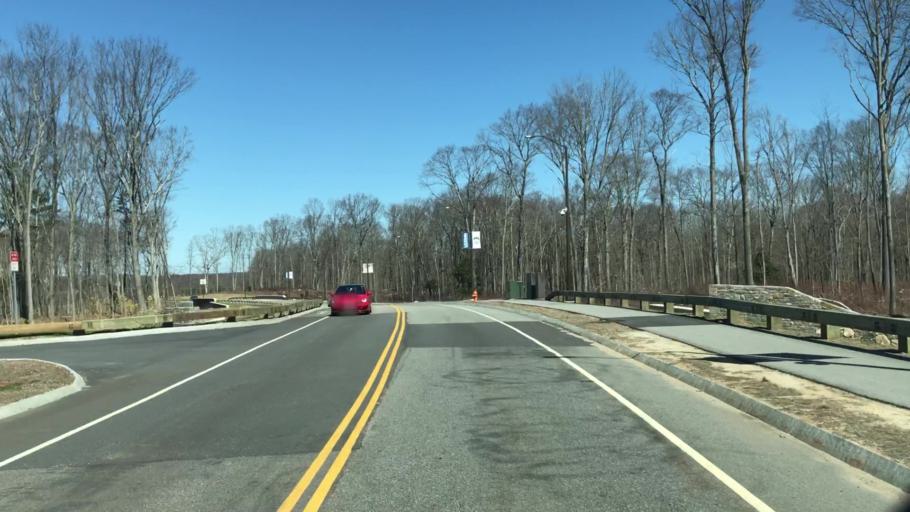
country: US
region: Connecticut
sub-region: Tolland County
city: Storrs
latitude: 41.8218
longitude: -72.2659
